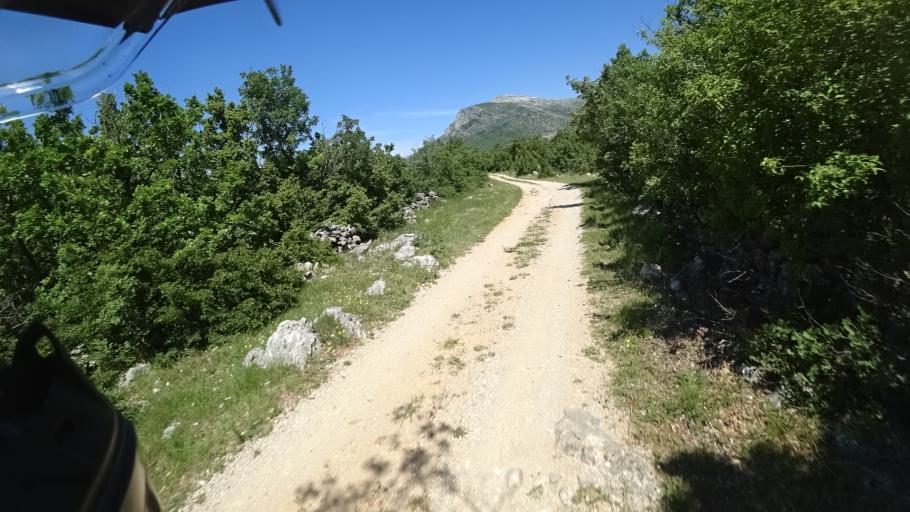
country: BA
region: Federation of Bosnia and Herzegovina
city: Bosansko Grahovo
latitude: 43.9933
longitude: 16.4174
